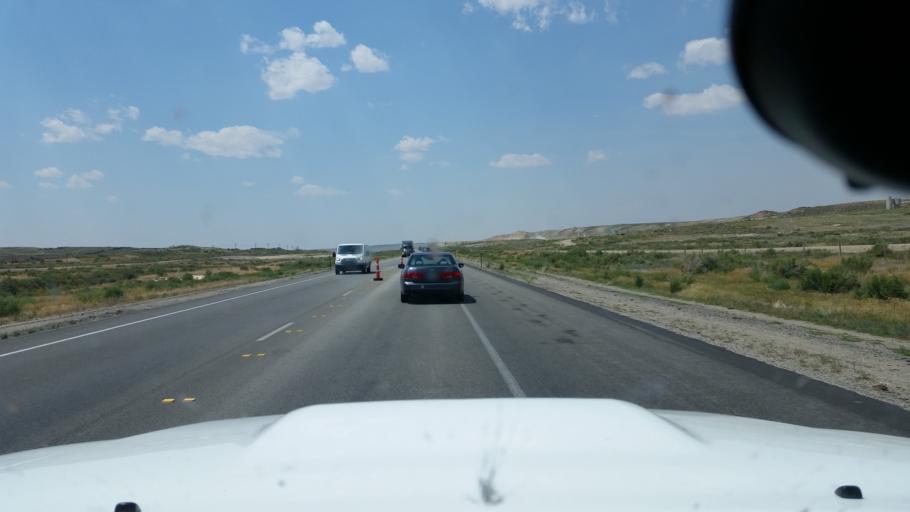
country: US
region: Wyoming
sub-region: Carbon County
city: Rawlins
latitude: 41.7060
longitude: -107.8543
